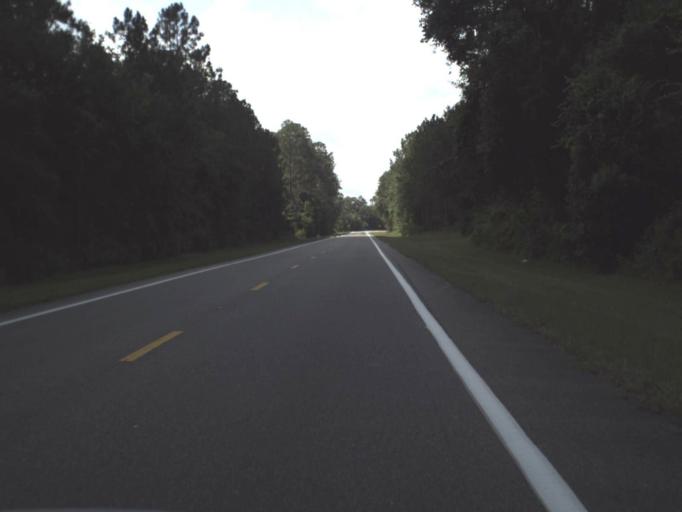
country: US
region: Florida
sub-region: Union County
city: Lake Butler
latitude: 30.0837
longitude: -82.2161
